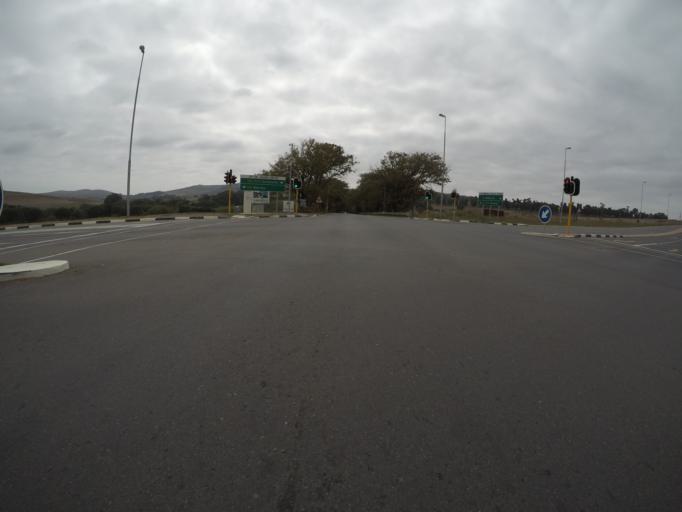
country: ZA
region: Western Cape
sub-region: City of Cape Town
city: Kraaifontein
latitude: -33.8498
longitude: 18.6293
